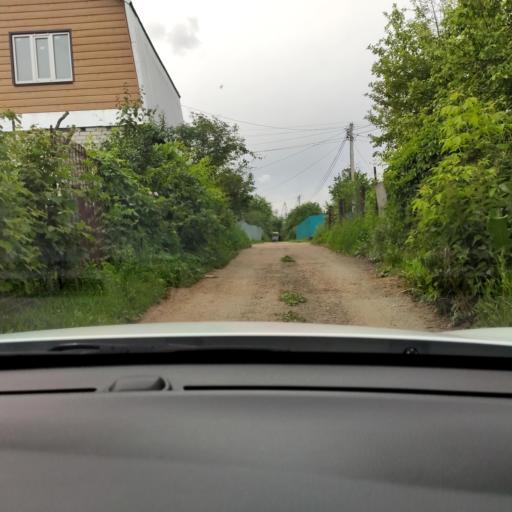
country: RU
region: Tatarstan
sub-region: Gorod Kazan'
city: Kazan
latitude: 55.8708
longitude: 49.1057
